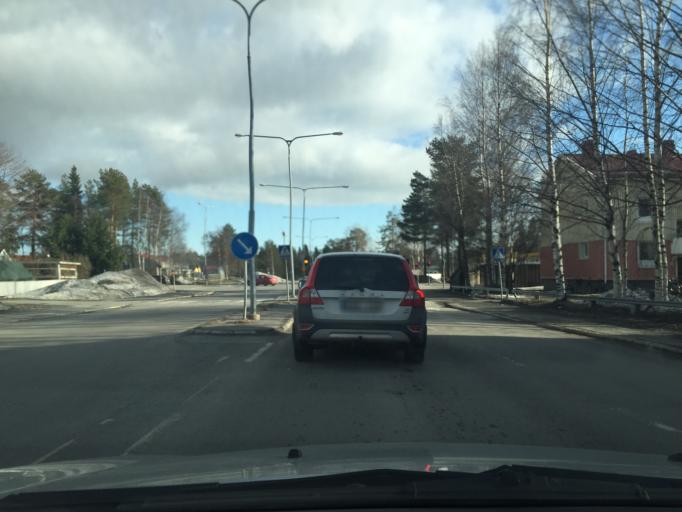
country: SE
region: Norrbotten
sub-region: Lulea Kommun
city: Lulea
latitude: 65.5838
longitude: 22.2072
